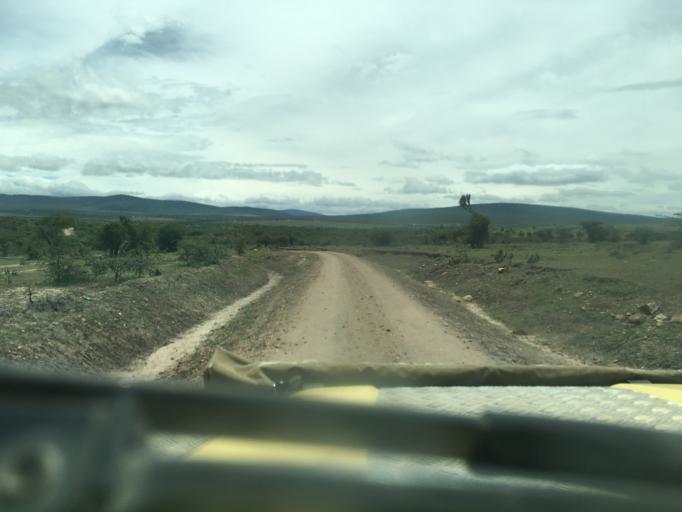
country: TZ
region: Mara
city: Mugumu
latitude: -1.9434
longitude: 35.4591
